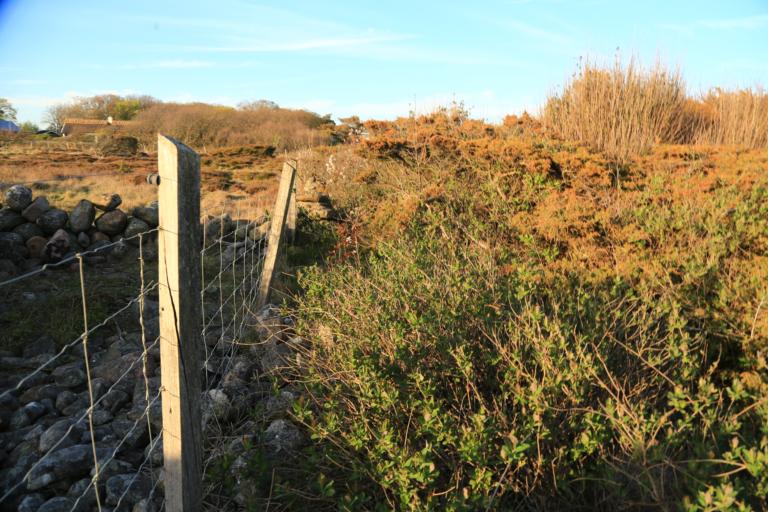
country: SE
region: Halland
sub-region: Varbergs Kommun
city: Traslovslage
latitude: 57.0379
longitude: 12.2968
